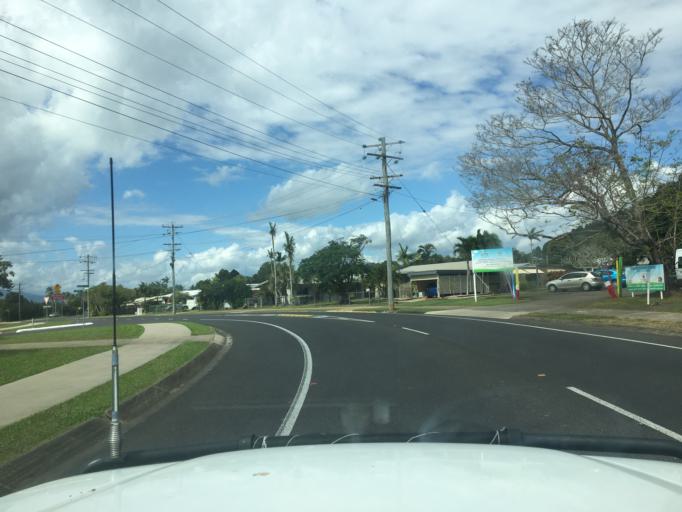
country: AU
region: Queensland
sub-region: Cairns
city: Woree
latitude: -16.9647
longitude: 145.7399
